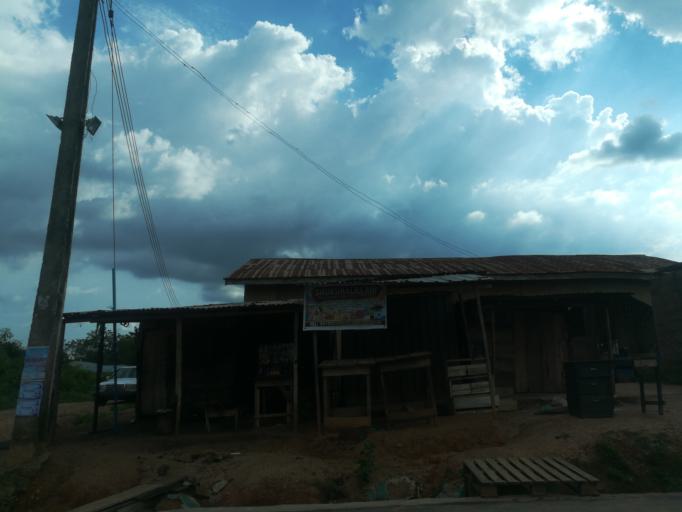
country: NG
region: Oyo
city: Ibadan
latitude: 7.4083
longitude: 3.8262
